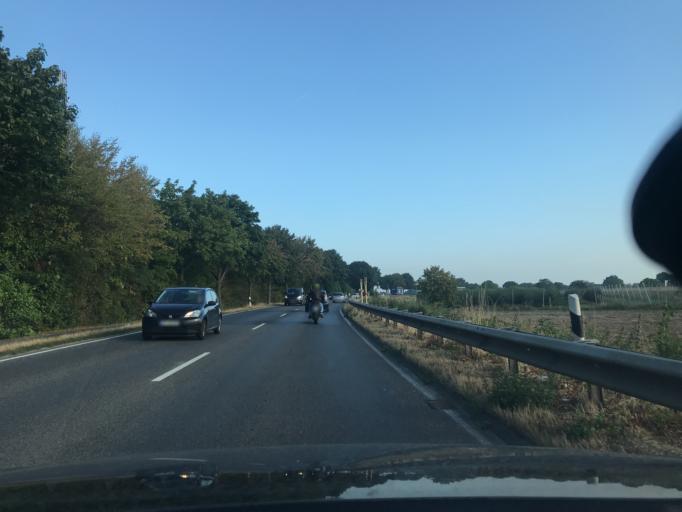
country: DE
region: North Rhine-Westphalia
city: Tonisvorst
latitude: 51.3200
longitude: 6.4714
